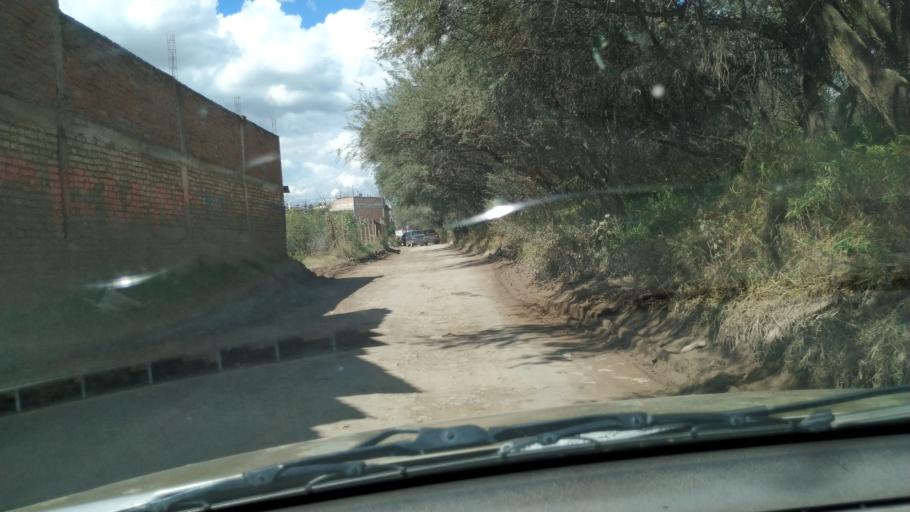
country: MX
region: Guanajuato
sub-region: Leon
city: Medina
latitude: 21.1420
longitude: -101.6282
